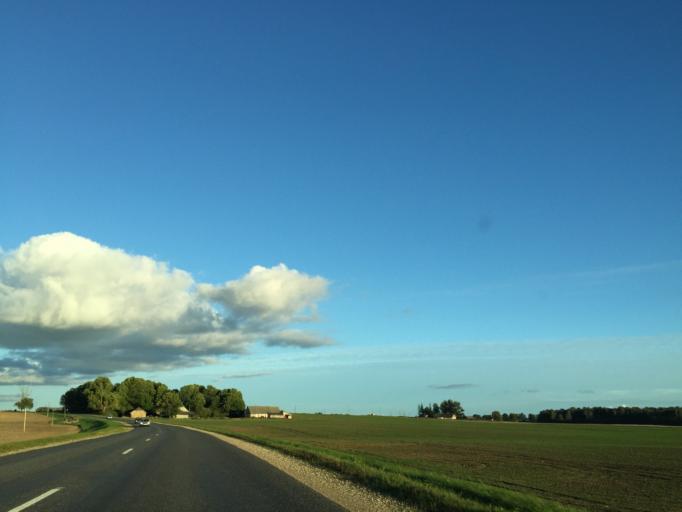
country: LV
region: Saldus Rajons
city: Saldus
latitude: 56.7143
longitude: 22.3989
